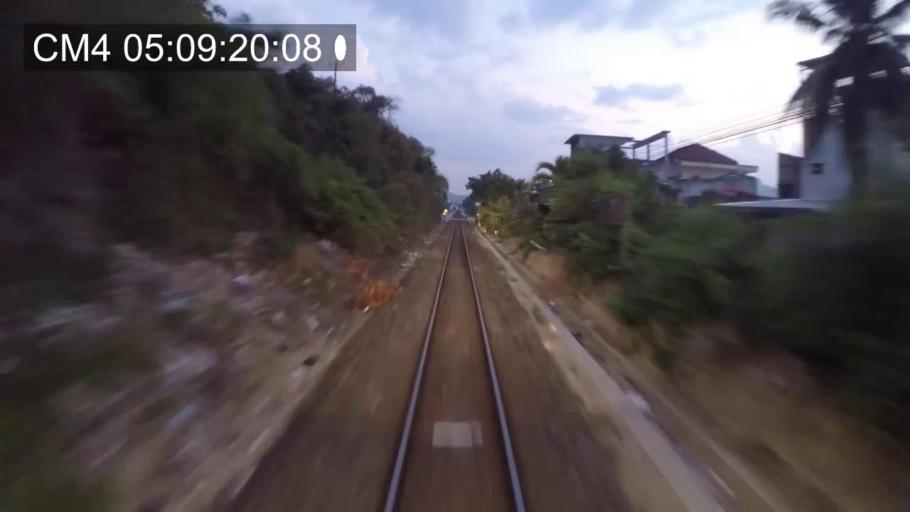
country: VN
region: Khanh Hoa
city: Nha Trang
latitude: 12.2998
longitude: 109.1858
